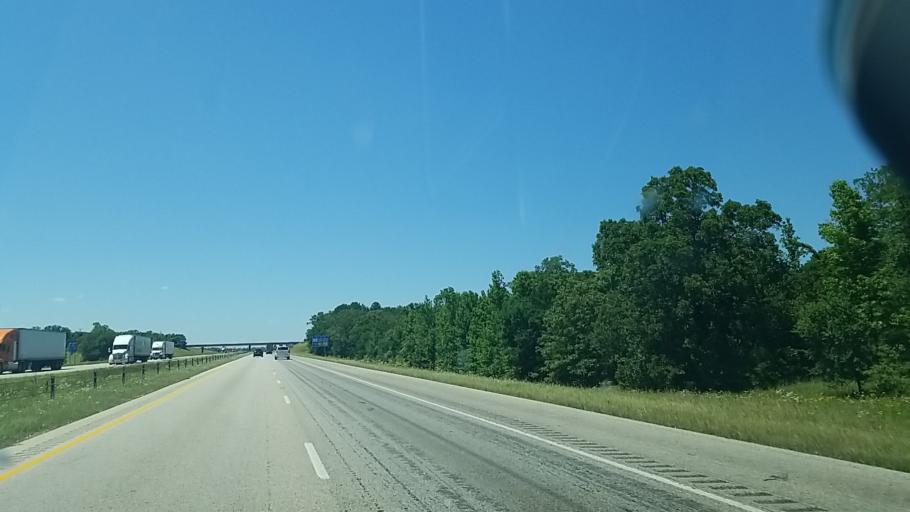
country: US
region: Texas
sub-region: Leon County
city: Buffalo
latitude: 31.4410
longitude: -96.0669
